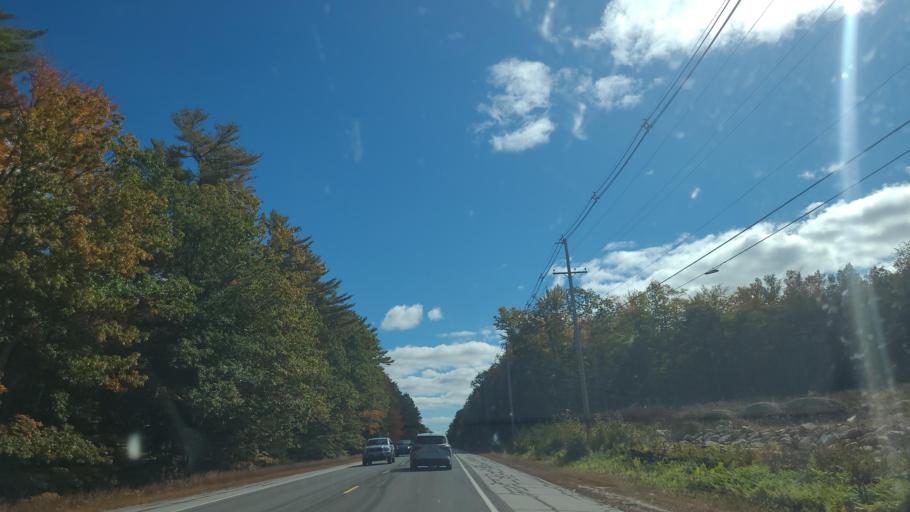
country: US
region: Maine
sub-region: Cumberland County
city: Bridgton
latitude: 43.9825
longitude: -70.6320
